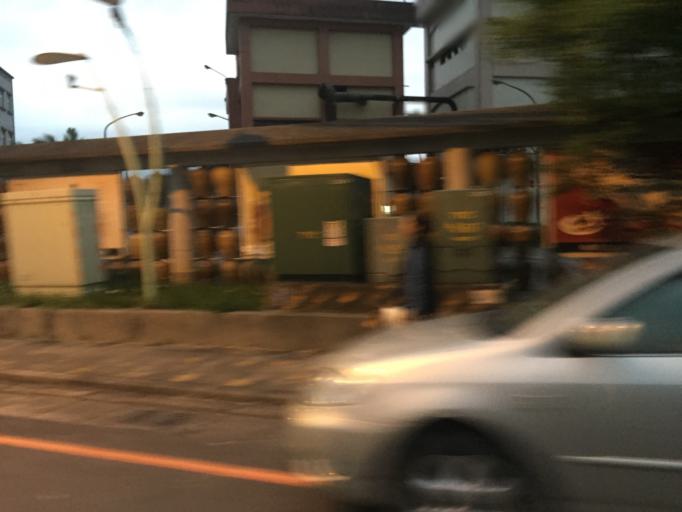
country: TW
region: Taiwan
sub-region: Yilan
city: Yilan
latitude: 24.7564
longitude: 121.7473
